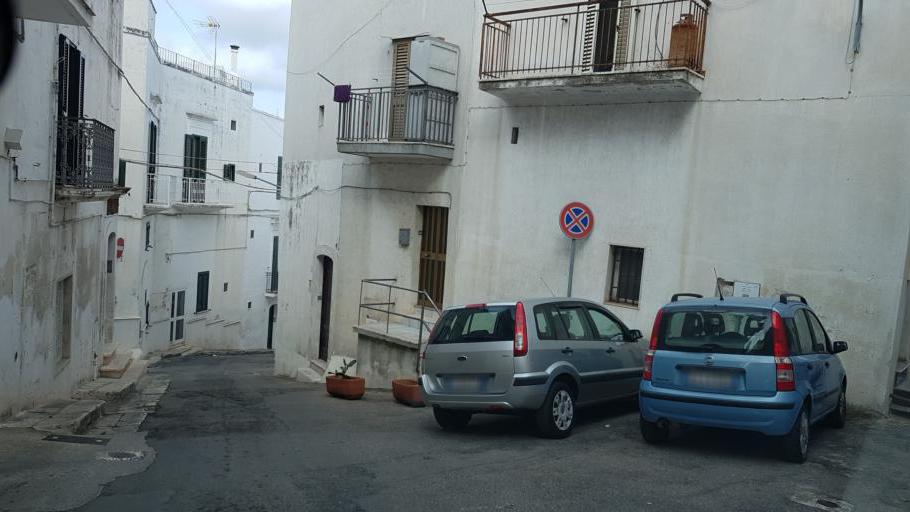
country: IT
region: Apulia
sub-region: Provincia di Brindisi
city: Ostuni
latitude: 40.7315
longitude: 17.5769
